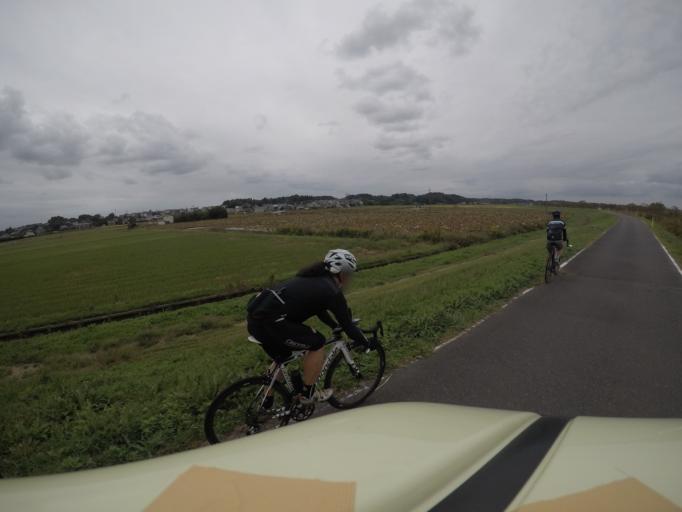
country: JP
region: Ibaraki
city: Ami
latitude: 36.0347
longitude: 140.2738
